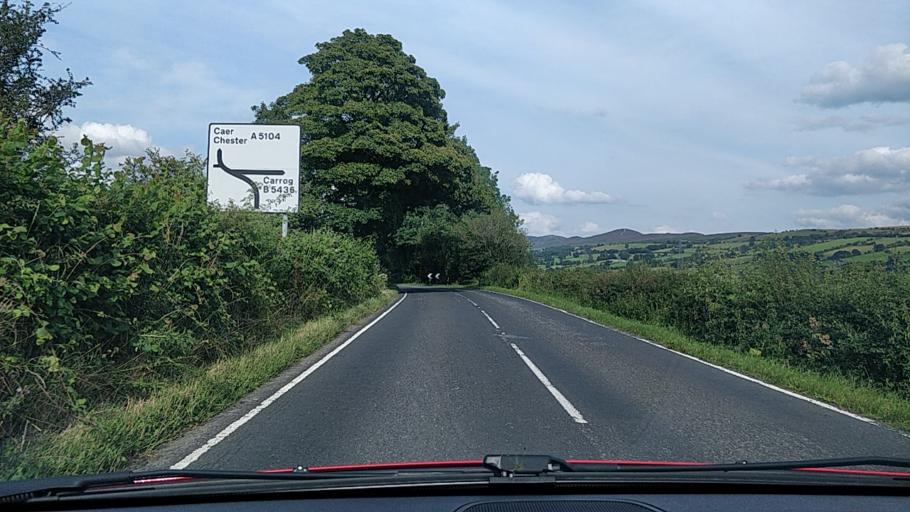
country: GB
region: Wales
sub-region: Denbighshire
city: Corwen
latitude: 53.0005
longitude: -3.3404
